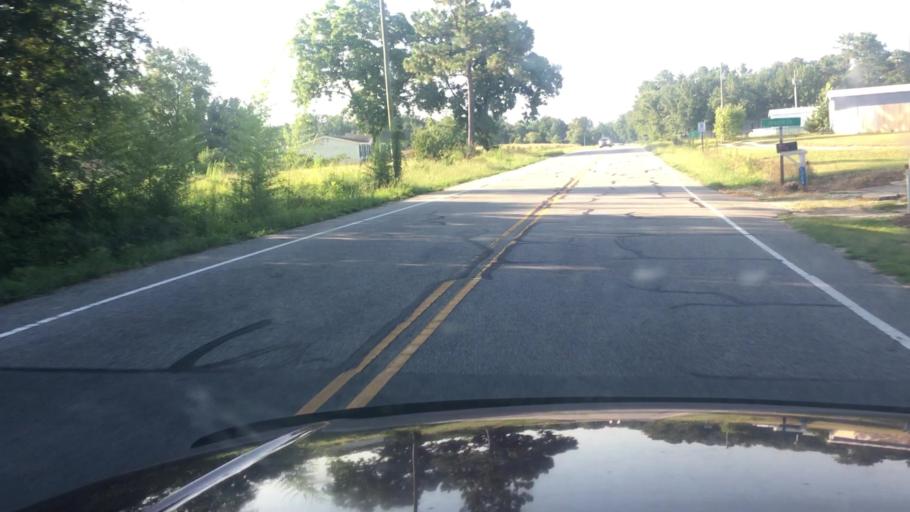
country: US
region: North Carolina
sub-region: Robeson County
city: Saint Pauls
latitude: 34.8370
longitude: -78.8945
